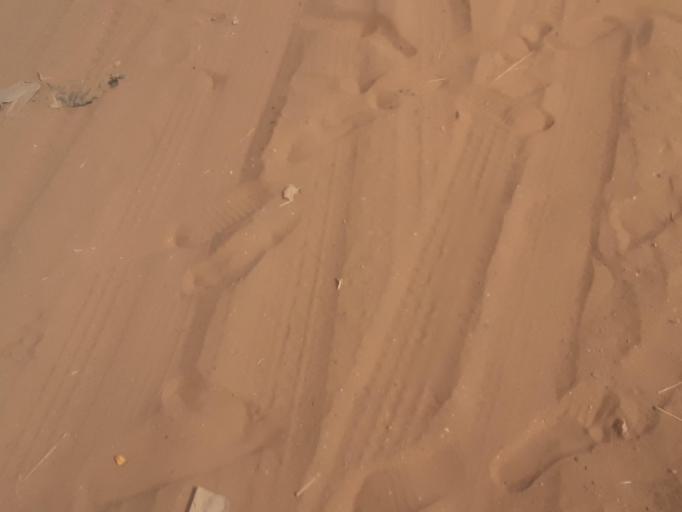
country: ZM
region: Lusaka
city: Lusaka
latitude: -15.3554
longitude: 28.2951
